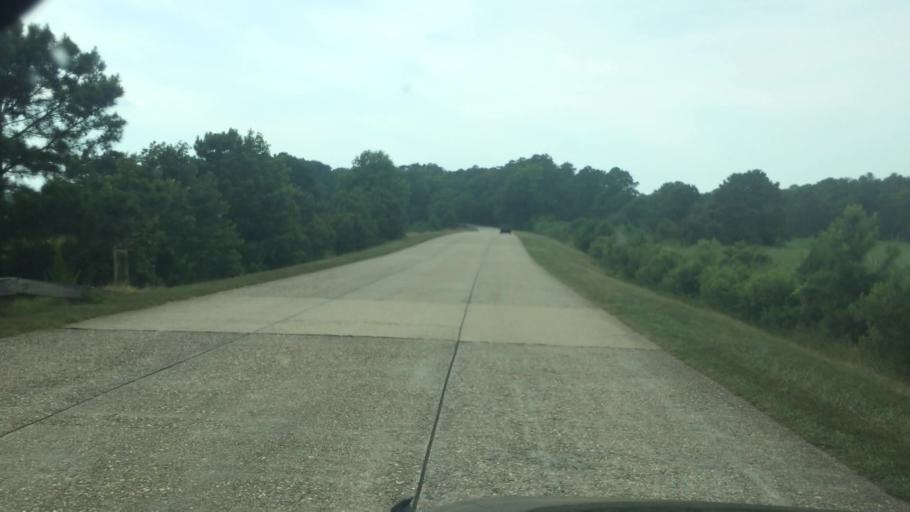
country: US
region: Virginia
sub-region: James City County
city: Williamsburg
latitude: 37.2152
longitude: -76.7450
